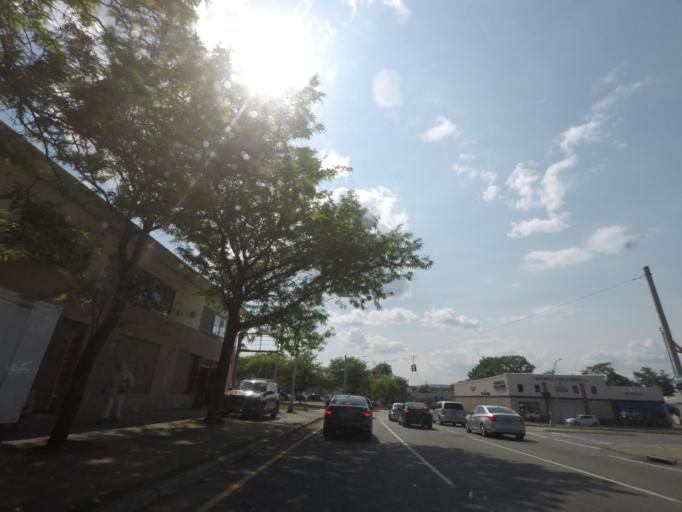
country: US
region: New York
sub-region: Dutchess County
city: Poughkeepsie
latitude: 41.7024
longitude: -73.9200
